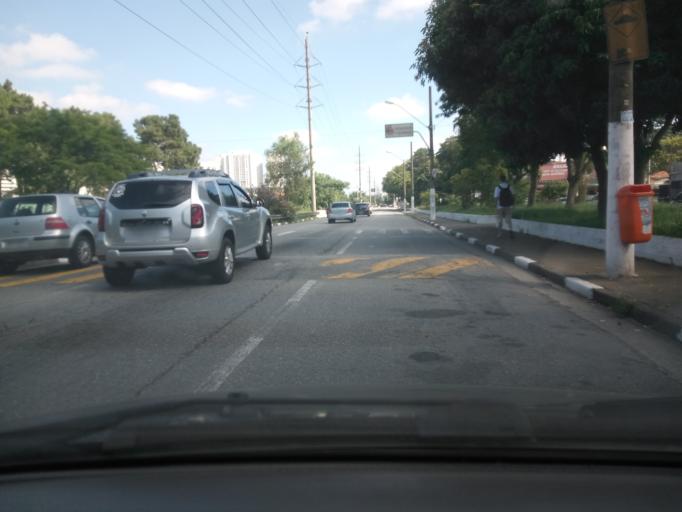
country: BR
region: Sao Paulo
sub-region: Sao Bernardo Do Campo
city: Sao Bernardo do Campo
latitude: -23.7032
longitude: -46.5764
